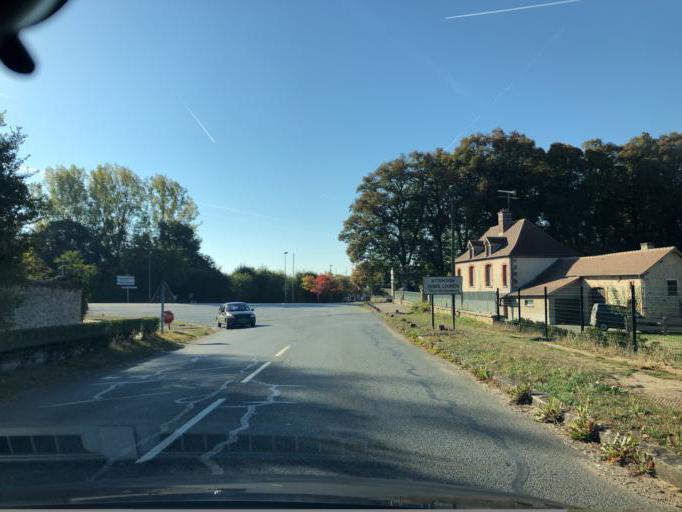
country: FR
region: Ile-de-France
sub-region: Departement des Yvelines
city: Rambouillet
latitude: 48.6579
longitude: 1.8206
